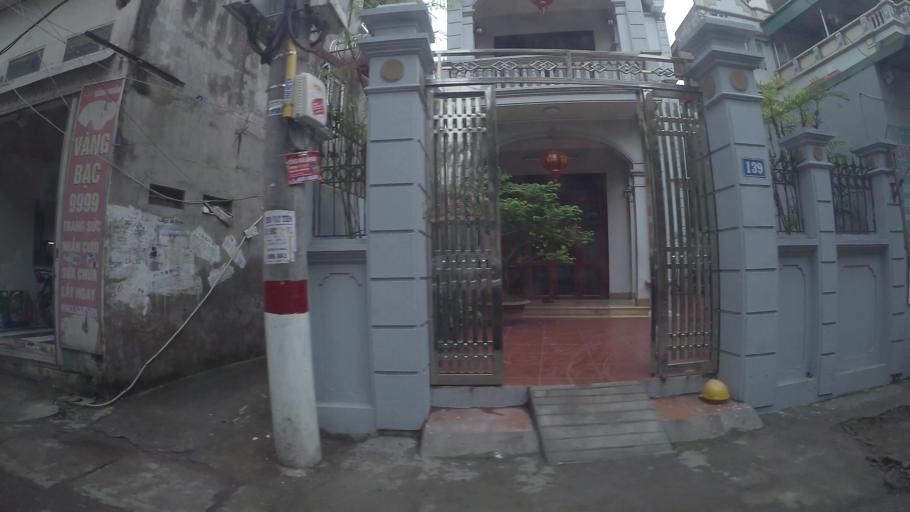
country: VN
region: Ha Noi
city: Van Dien
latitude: 20.9705
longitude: 105.8699
